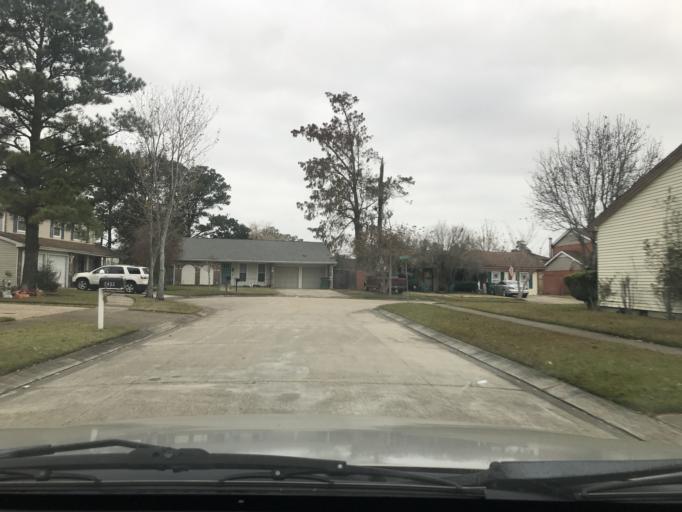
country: US
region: Louisiana
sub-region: Jefferson Parish
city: Woodmere
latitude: 29.8619
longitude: -90.0785
